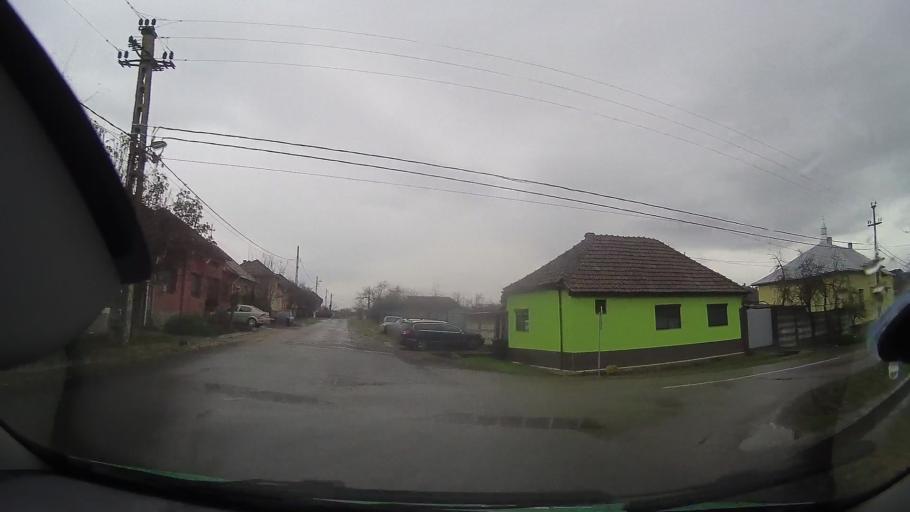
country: RO
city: Capalna
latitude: 46.7361
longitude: 22.1030
